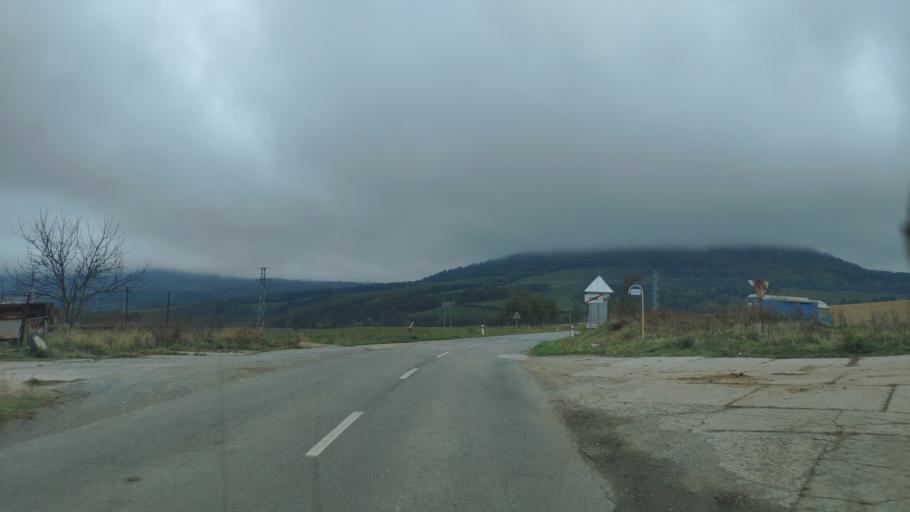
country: SK
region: Presovsky
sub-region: Okres Presov
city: Presov
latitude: 49.1037
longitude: 21.2373
